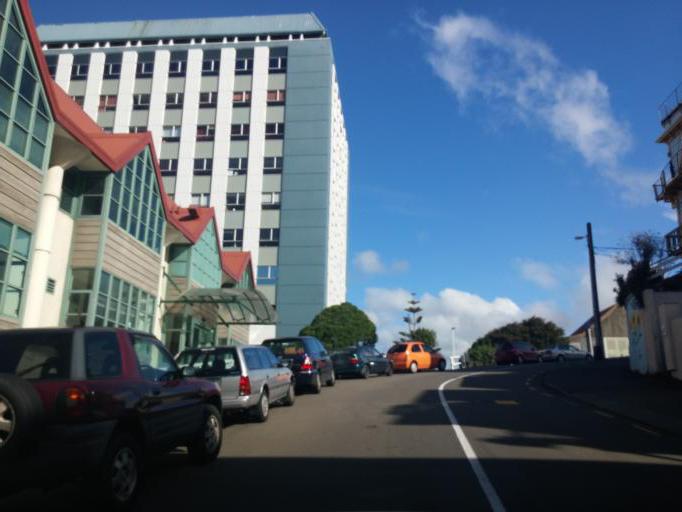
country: NZ
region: Wellington
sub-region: Wellington City
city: Wellington
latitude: -41.2906
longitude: 174.7730
